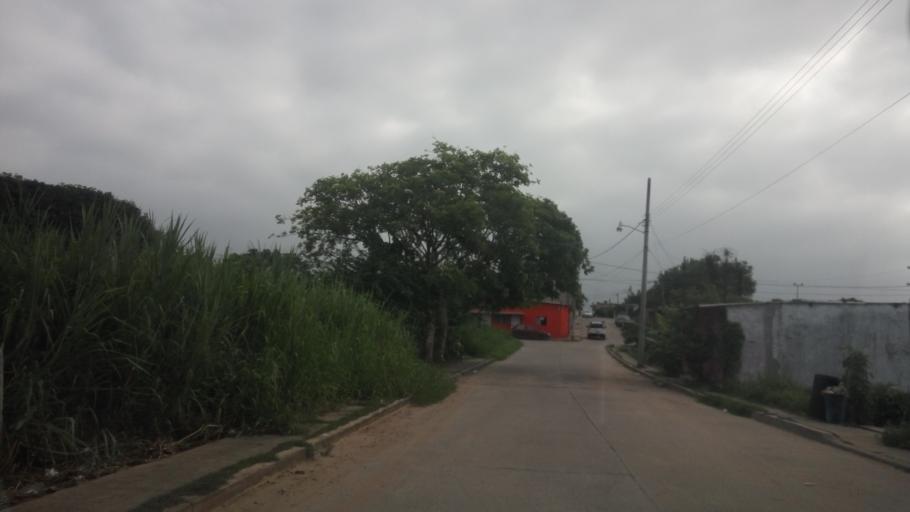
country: MX
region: Chiapas
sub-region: Reforma
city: El Carmen (El Limon)
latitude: 17.8583
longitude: -93.1527
